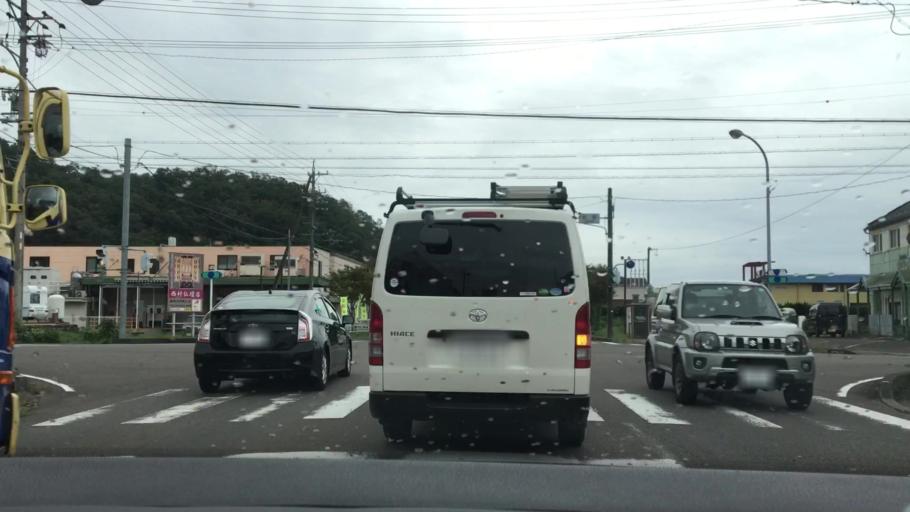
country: JP
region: Gifu
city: Mino
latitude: 35.5202
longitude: 136.8557
